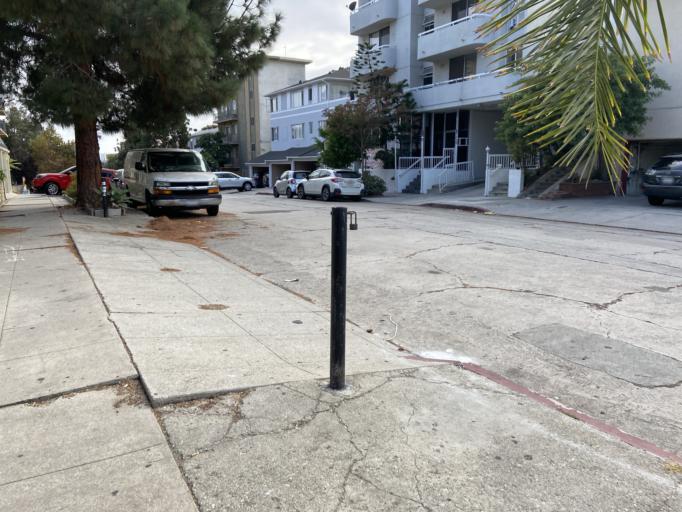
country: US
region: California
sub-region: Los Angeles County
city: Westwood, Los Angeles
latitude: 34.0682
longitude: -118.4515
